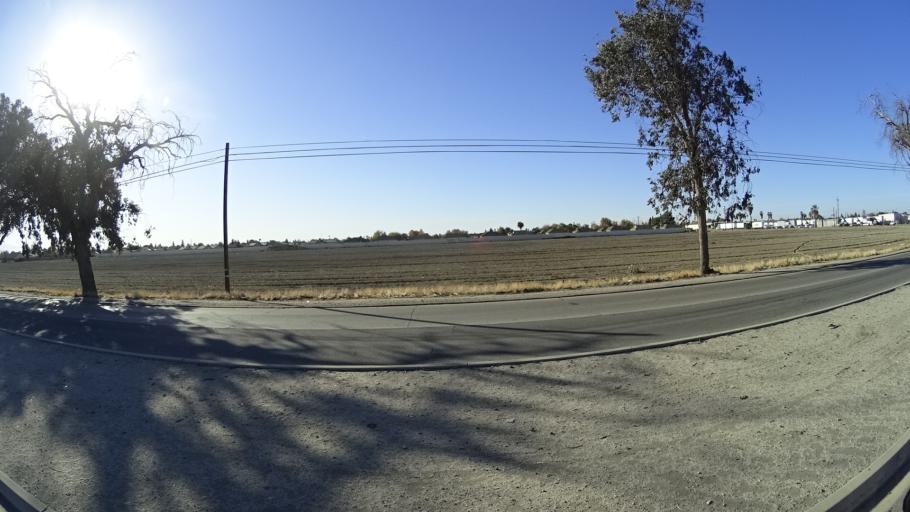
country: US
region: California
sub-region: Kern County
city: Greenfield
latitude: 35.3017
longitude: -119.0030
